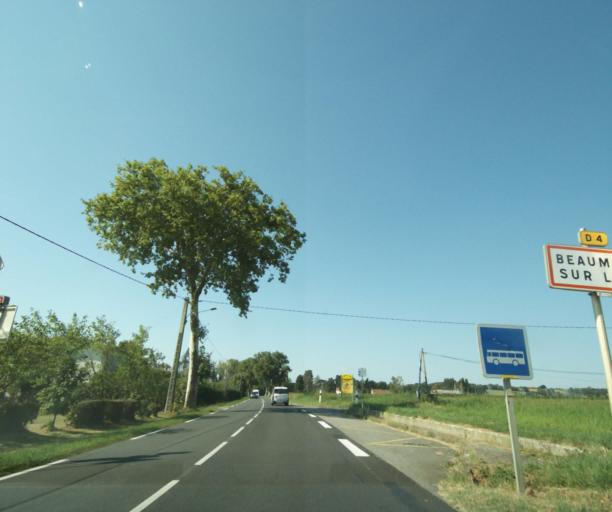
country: FR
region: Midi-Pyrenees
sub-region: Departement de la Haute-Garonne
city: Beaumont-sur-Leze
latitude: 43.3894
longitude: 1.3506
